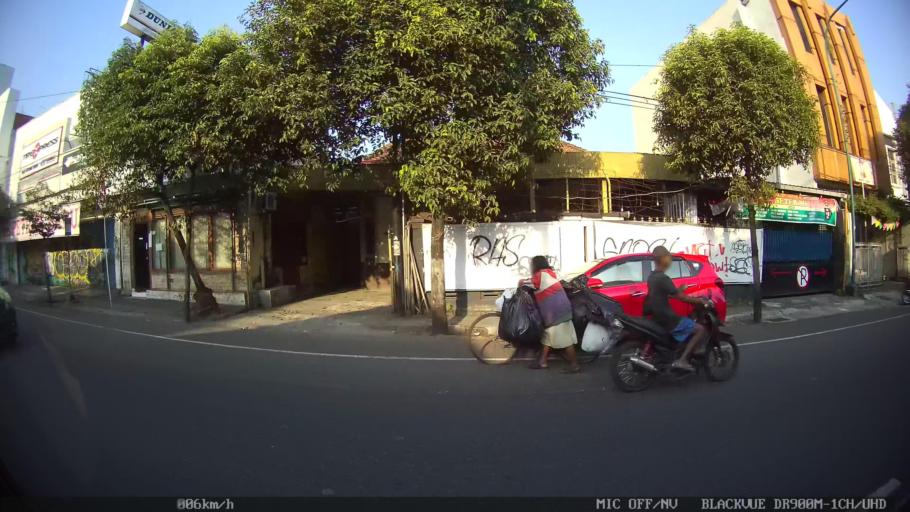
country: ID
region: Daerah Istimewa Yogyakarta
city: Yogyakarta
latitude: -7.8048
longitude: 110.3695
